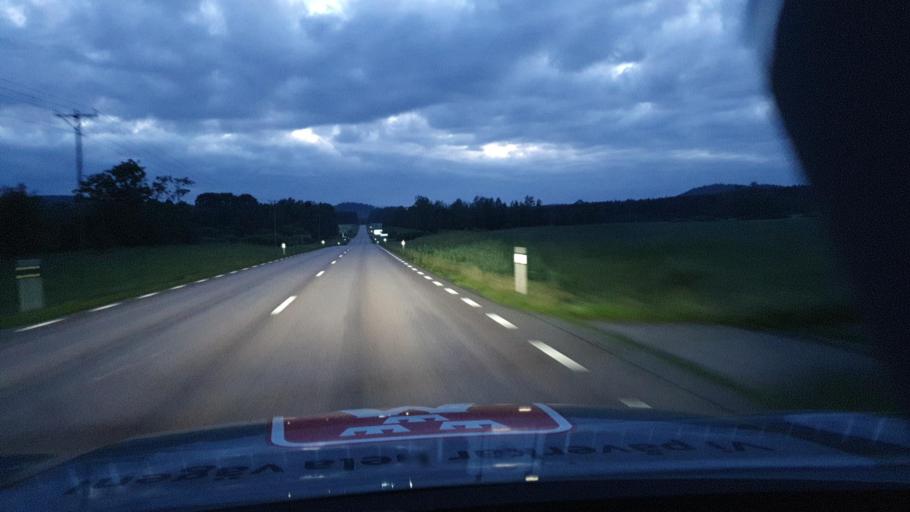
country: SE
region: OErebro
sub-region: Karlskoga Kommun
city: Karlskoga
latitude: 59.4364
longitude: 14.4095
